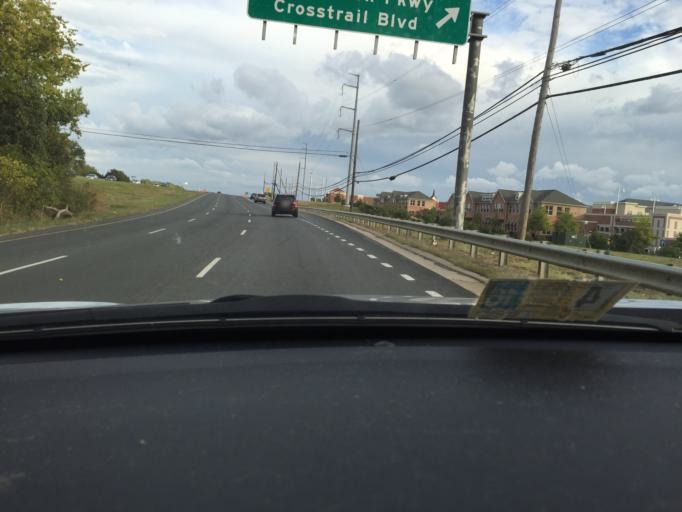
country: US
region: Virginia
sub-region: Loudoun County
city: Belmont
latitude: 39.0921
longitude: -77.5252
